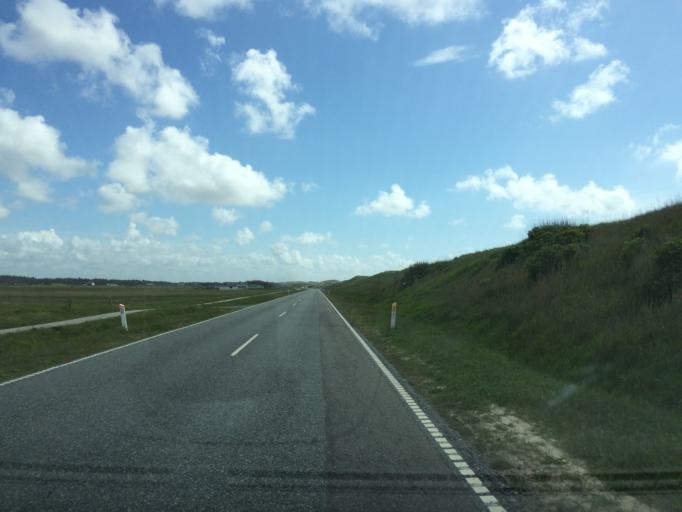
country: DK
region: Central Jutland
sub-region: Holstebro Kommune
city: Ulfborg
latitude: 56.3300
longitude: 8.1230
